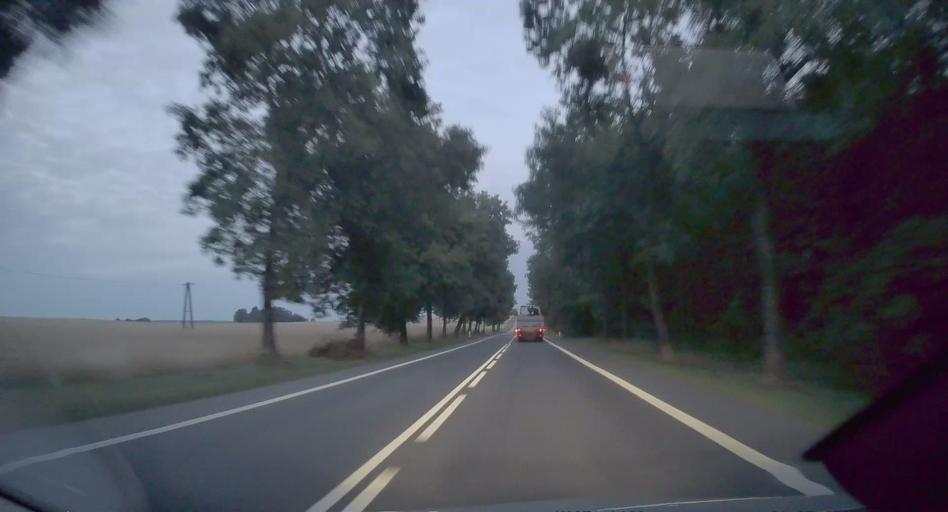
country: PL
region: Silesian Voivodeship
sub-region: Powiat klobucki
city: Opatow
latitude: 50.9430
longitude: 18.8373
